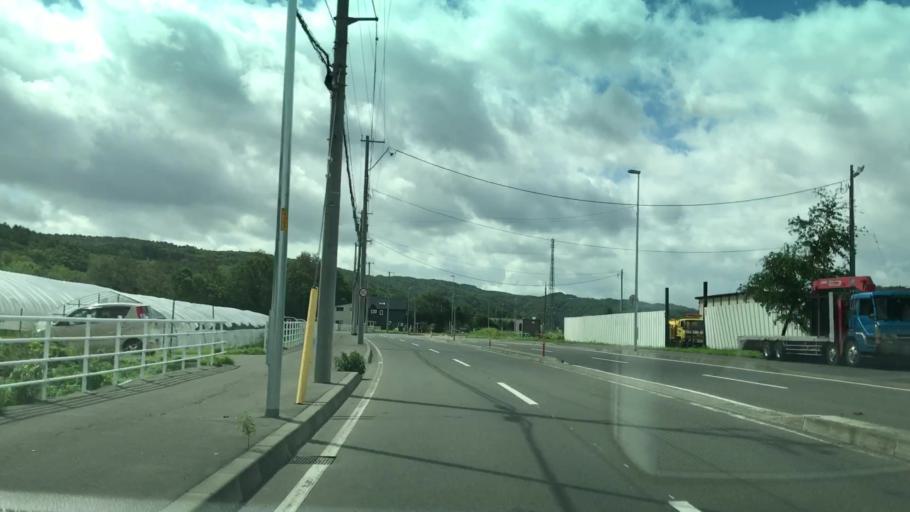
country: JP
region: Hokkaido
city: Kitahiroshima
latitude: 42.9571
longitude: 141.4544
